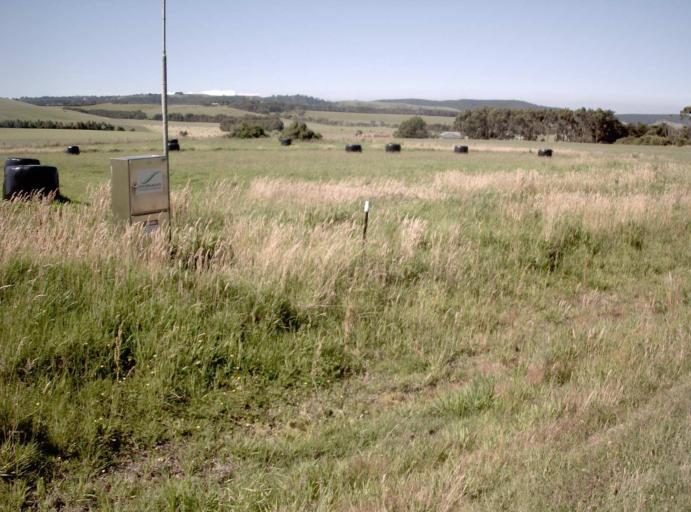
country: AU
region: Victoria
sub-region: Latrobe
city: Morwell
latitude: -38.6631
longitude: 146.4481
